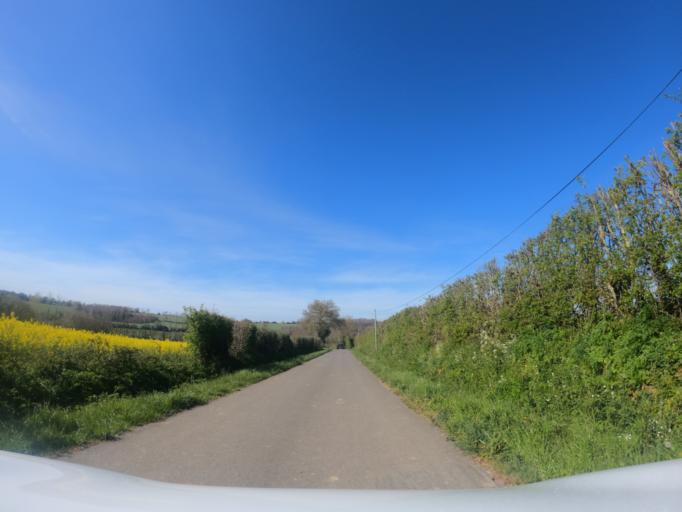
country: FR
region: Pays de la Loire
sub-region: Departement de la Vendee
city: La Tardiere
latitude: 46.6972
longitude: -0.7424
